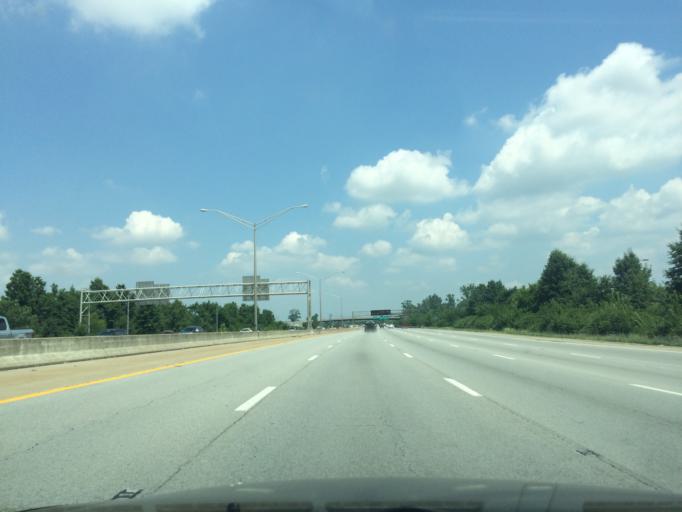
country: US
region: Kentucky
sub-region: Jefferson County
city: Heritage Creek
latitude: 38.1629
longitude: -85.7207
